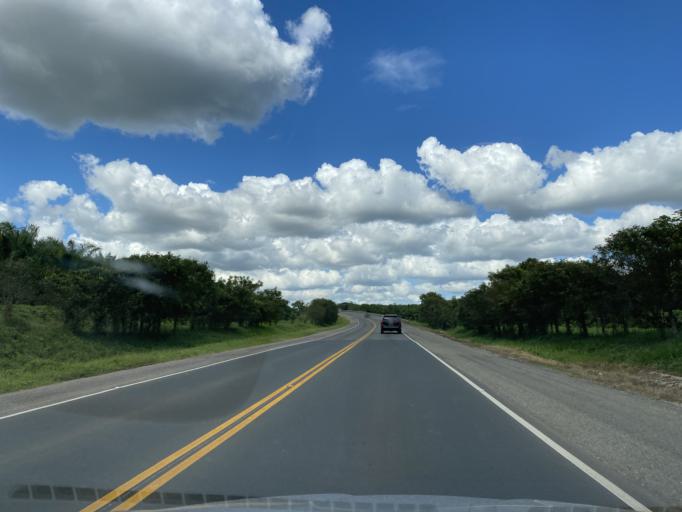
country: DO
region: Monte Plata
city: Monte Plata
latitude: 18.7109
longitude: -69.7555
